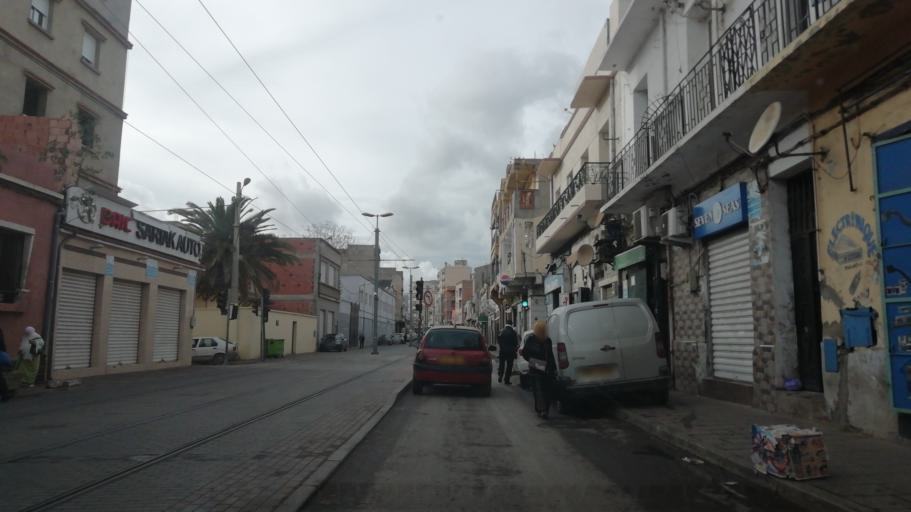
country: DZ
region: Oran
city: Oran
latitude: 35.6983
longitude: -0.6188
